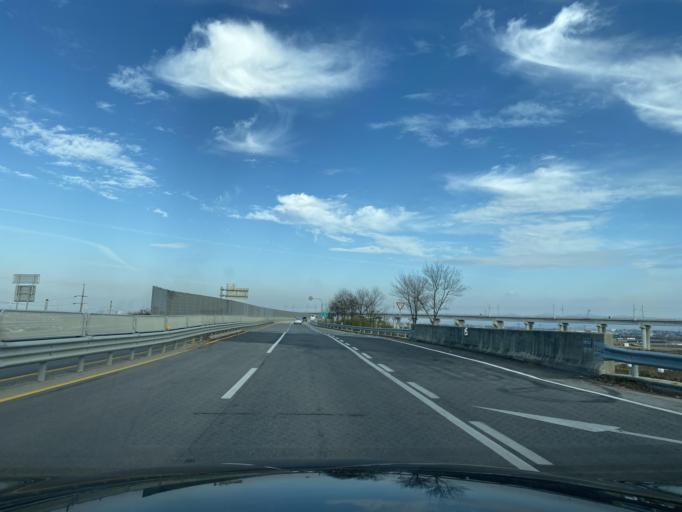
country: KR
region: Chungcheongnam-do
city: Hongsung
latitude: 36.6893
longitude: 126.7193
